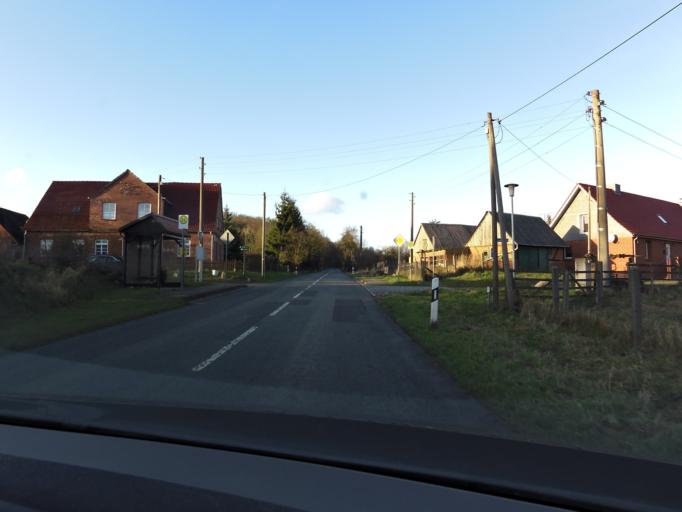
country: DE
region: Schleswig-Holstein
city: Kittlitz
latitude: 53.6667
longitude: 10.9596
